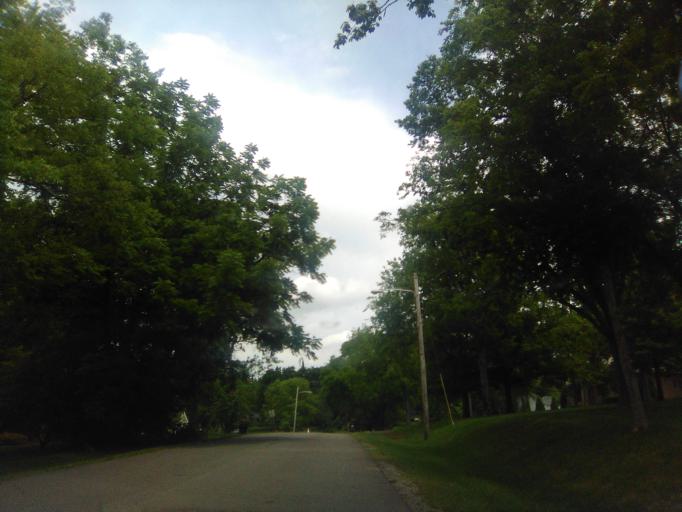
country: US
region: Tennessee
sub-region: Davidson County
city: Belle Meade
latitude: 36.1154
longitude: -86.8803
